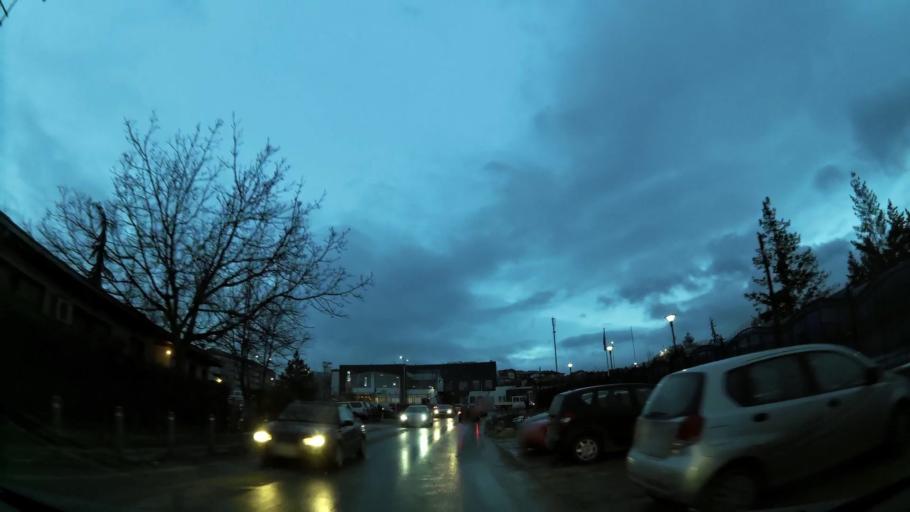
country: XK
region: Pristina
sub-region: Komuna e Prishtines
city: Pristina
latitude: 42.6455
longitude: 21.1671
